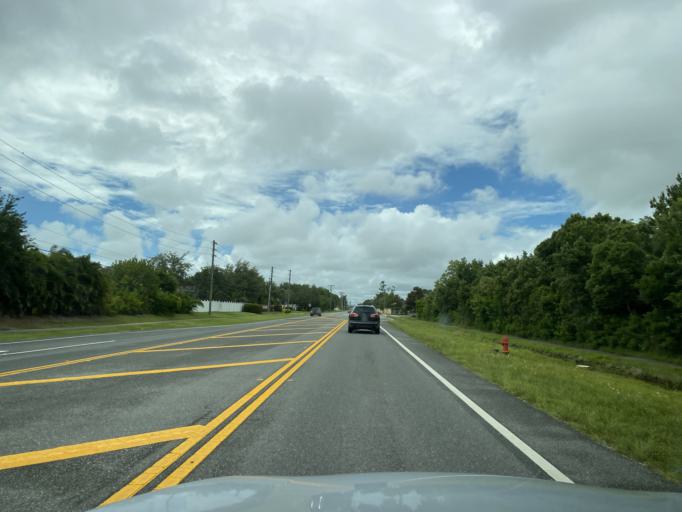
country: US
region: Florida
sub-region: Brevard County
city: West Melbourne
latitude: 28.0569
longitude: -80.6540
